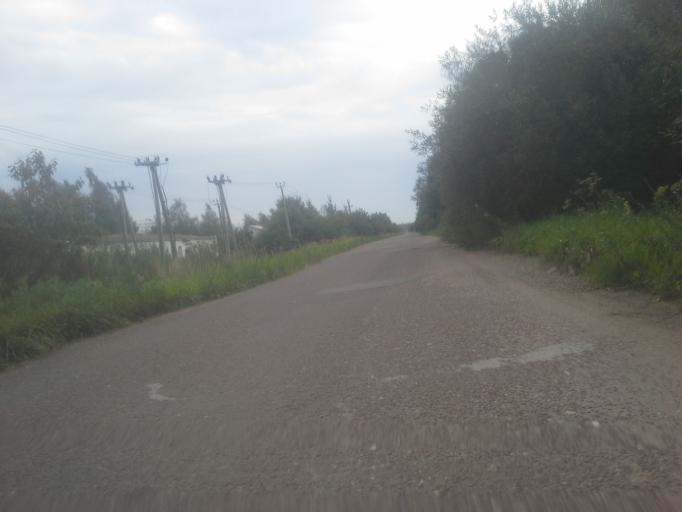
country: RU
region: Moskovskaya
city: Kievskij
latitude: 55.3828
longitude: 36.9079
